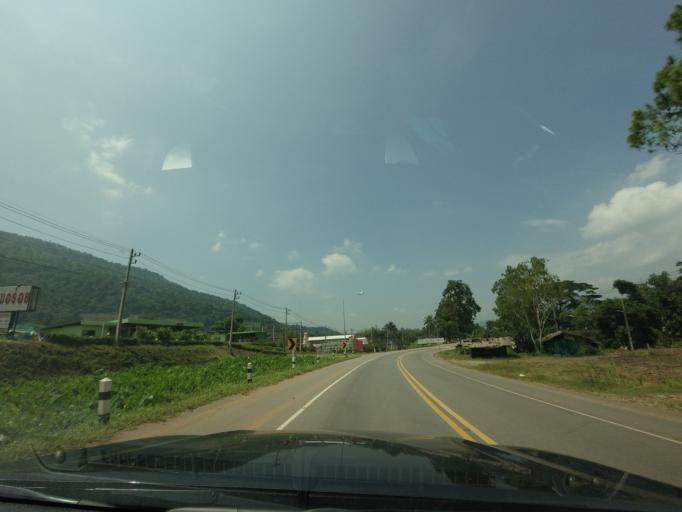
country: TH
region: Loei
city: Phu Ruea
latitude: 17.4562
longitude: 101.3954
